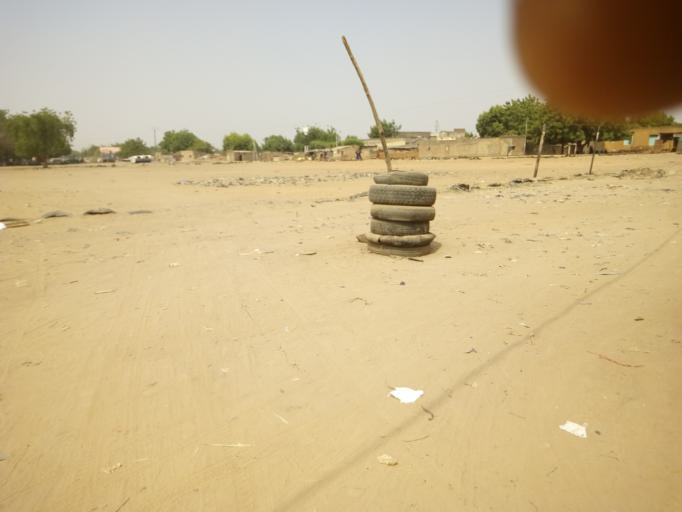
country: ML
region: Kayes
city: Kayes
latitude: 14.4361
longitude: -11.4382
